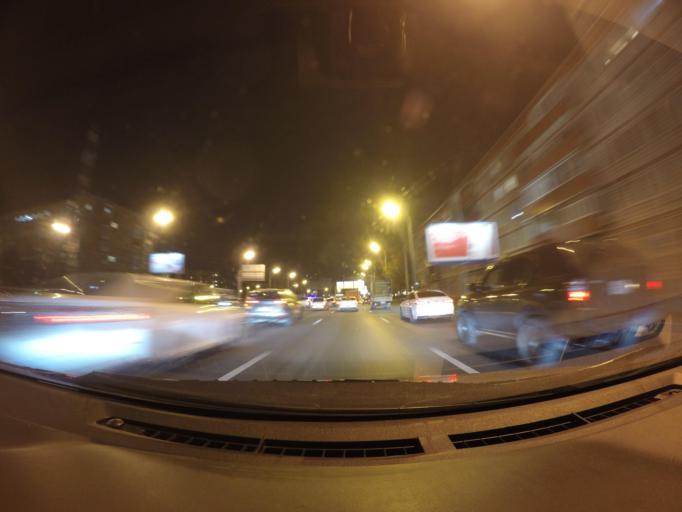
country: RU
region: Moskovskaya
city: Dorogomilovo
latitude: 55.7896
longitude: 37.5715
